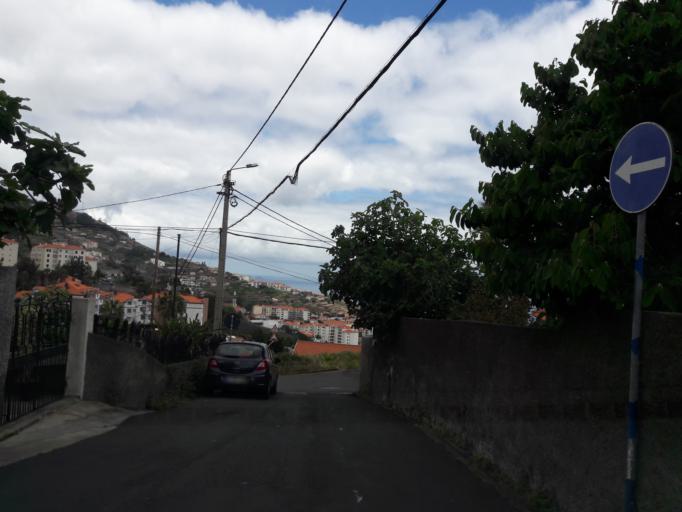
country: PT
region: Madeira
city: Canico
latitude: 32.6483
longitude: -16.8482
